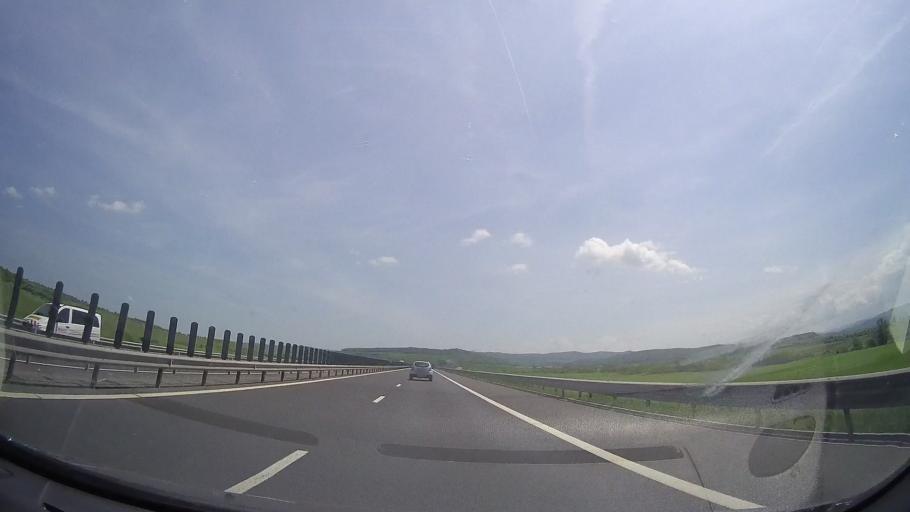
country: RO
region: Sibiu
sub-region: Oras Miercurea Sibiului
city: Miercurea Sibiului
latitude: 45.8919
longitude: 23.8273
